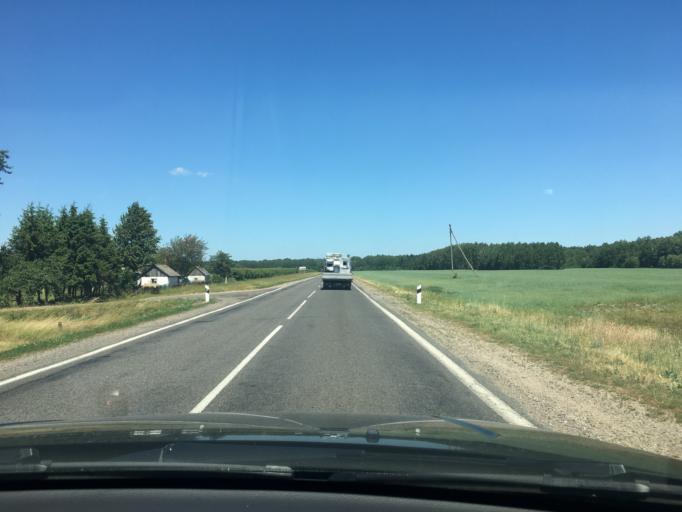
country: BY
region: Grodnenskaya
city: Iwye
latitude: 54.0661
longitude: 25.9115
